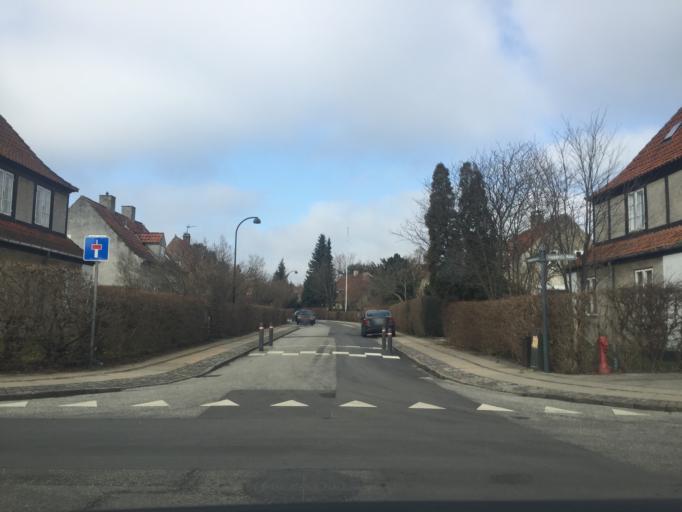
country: DK
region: Capital Region
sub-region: Gentofte Kommune
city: Charlottenlund
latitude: 55.7234
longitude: 12.5602
